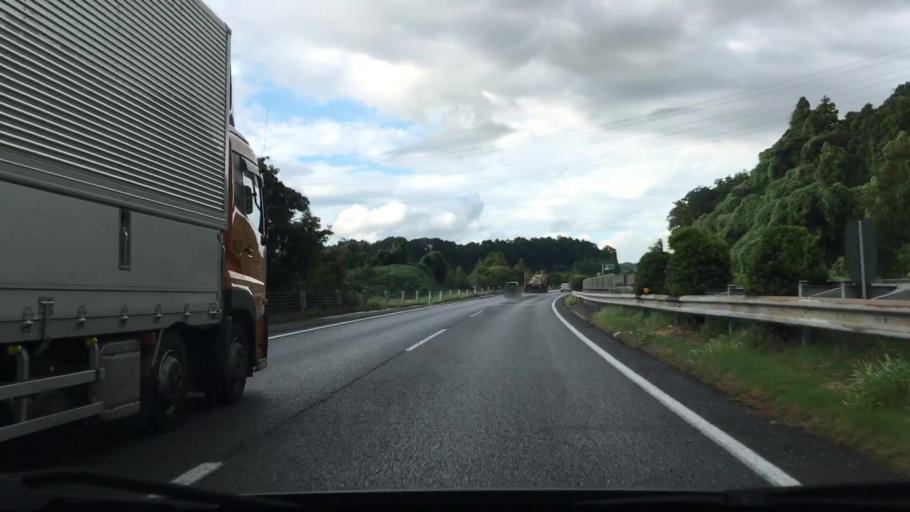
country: JP
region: Fukuoka
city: Koga
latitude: 33.7059
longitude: 130.4857
